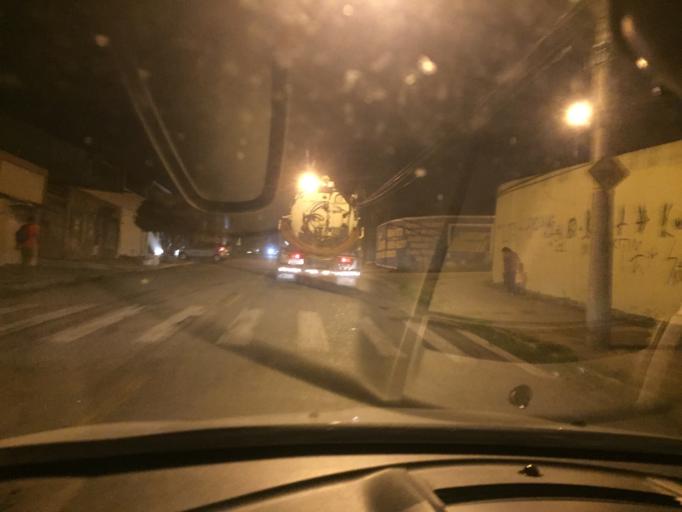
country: BR
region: Sao Paulo
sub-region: Varzea Paulista
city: Varzea Paulista
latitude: -23.2103
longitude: -46.8435
